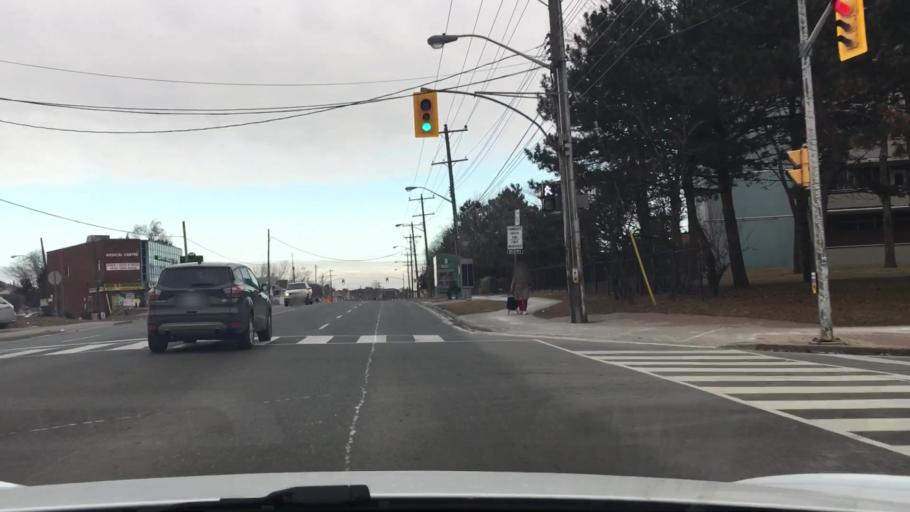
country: CA
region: Ontario
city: Scarborough
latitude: 43.7274
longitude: -79.2526
